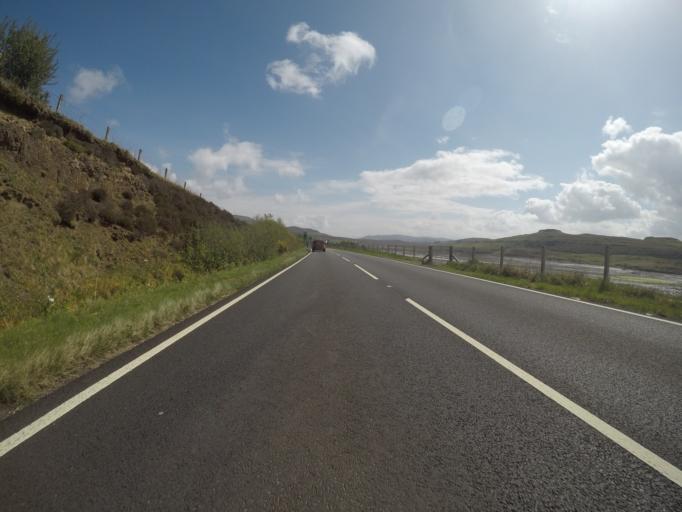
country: GB
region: Scotland
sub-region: Highland
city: Portree
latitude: 57.4901
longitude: -6.3161
